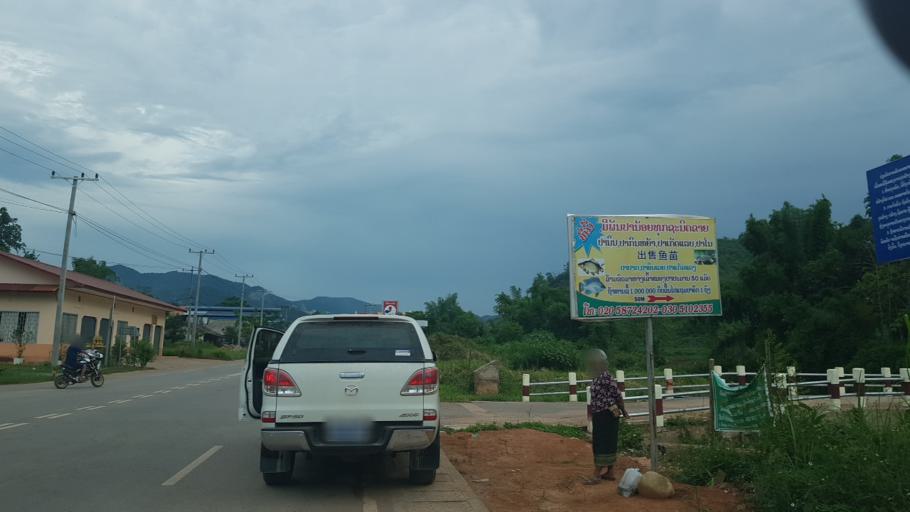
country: LA
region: Oudomxai
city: Muang Xay
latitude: 20.6537
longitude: 101.9769
